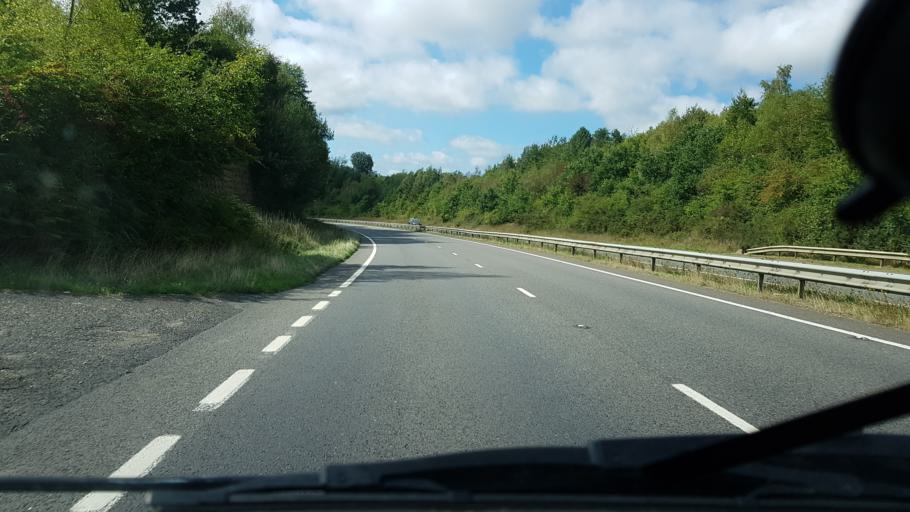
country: GB
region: England
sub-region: West Sussex
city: Broadfield
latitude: 51.0947
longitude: -0.2159
